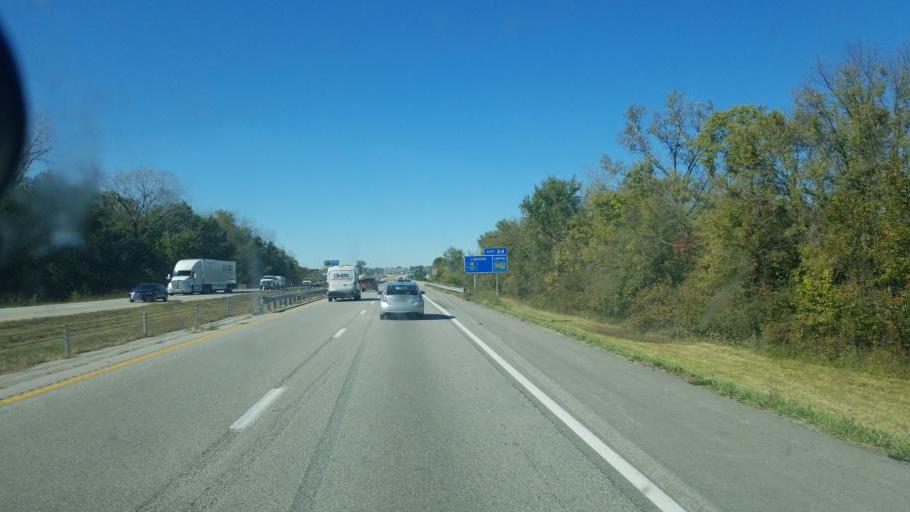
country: US
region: Missouri
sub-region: Jackson County
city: Grain Valley
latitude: 39.0205
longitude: -94.1802
